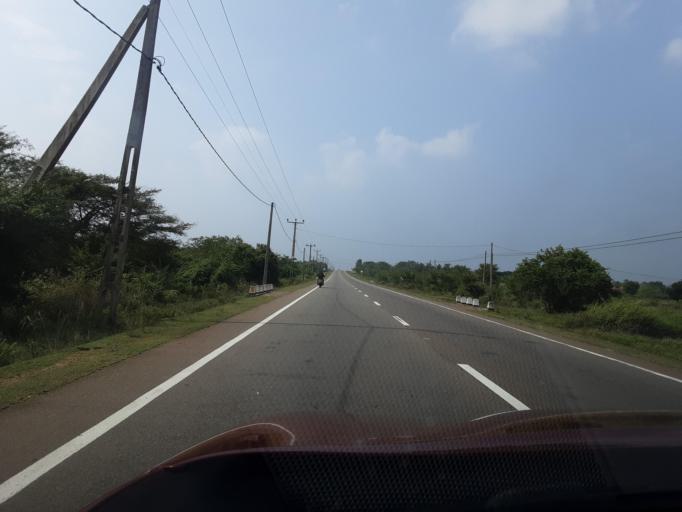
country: LK
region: Northern Province
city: Kilinochchi
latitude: 9.0852
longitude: 80.4771
